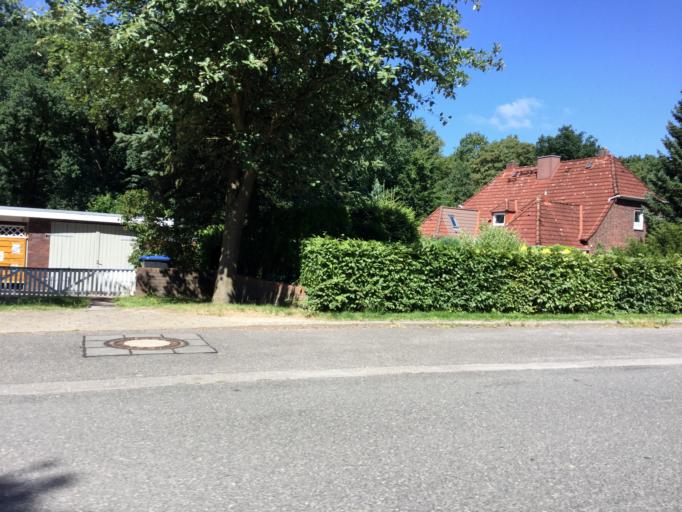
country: DE
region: Hamburg
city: Farmsen-Berne
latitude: 53.6308
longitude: 10.1329
